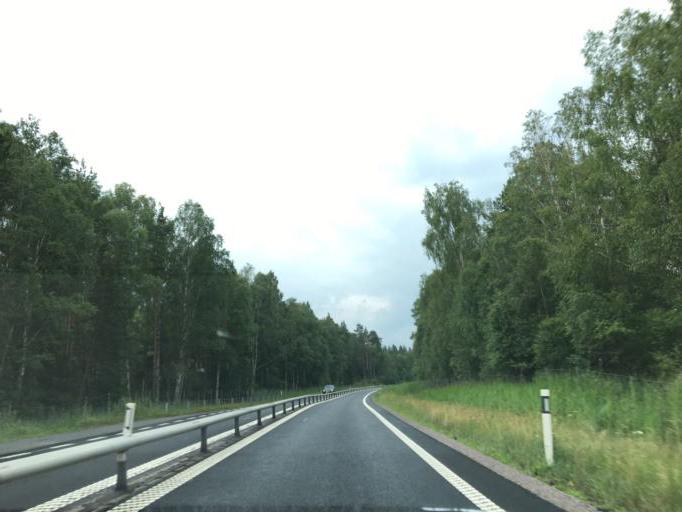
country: SE
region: Soedermanland
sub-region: Katrineholms Kommun
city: Katrineholm
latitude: 58.8796
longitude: 16.2017
